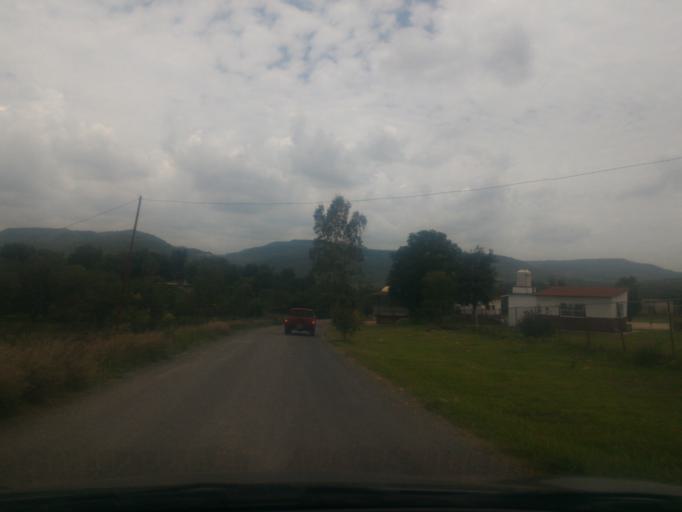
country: MX
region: Guanajuato
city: Ciudad Manuel Doblado
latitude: 20.8055
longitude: -102.0725
